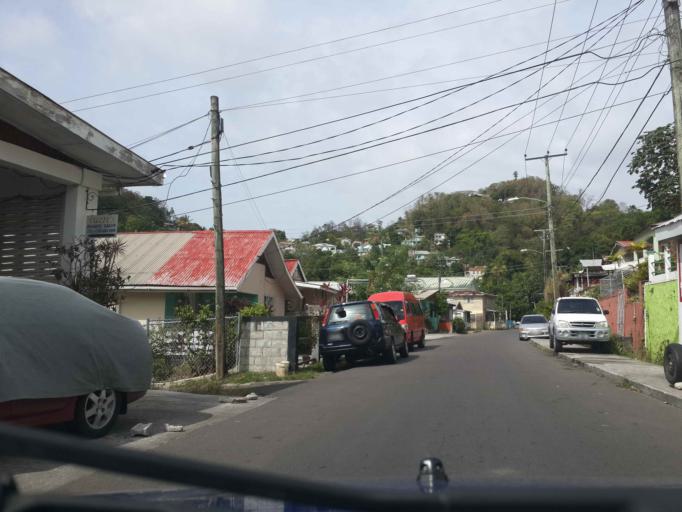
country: LC
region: Castries Quarter
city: Bisee
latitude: 14.0184
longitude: -60.9819
